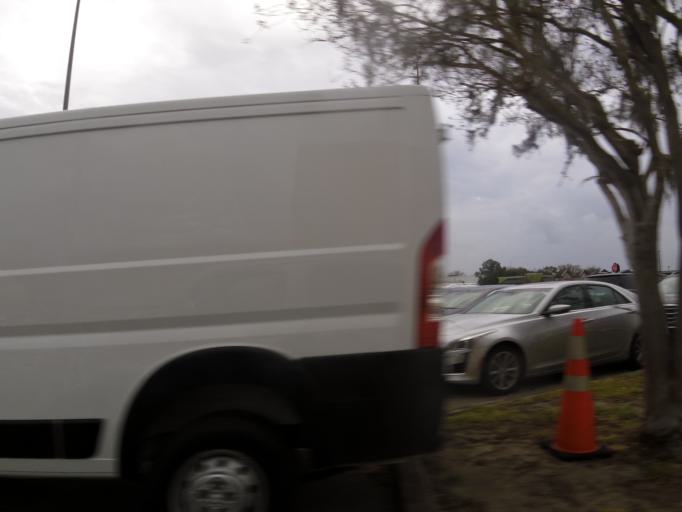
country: US
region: Florida
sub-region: Duval County
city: Jacksonville
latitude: 30.3228
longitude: -81.5540
